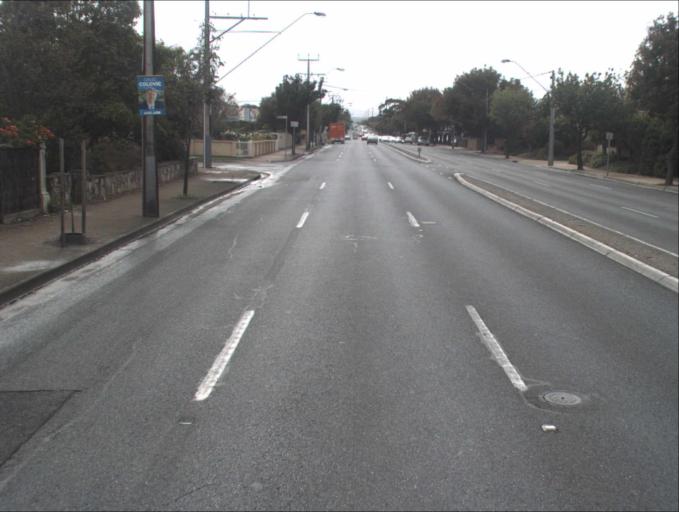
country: AU
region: South Australia
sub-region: Port Adelaide Enfield
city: Klemzig
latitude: -34.8861
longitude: 138.6175
